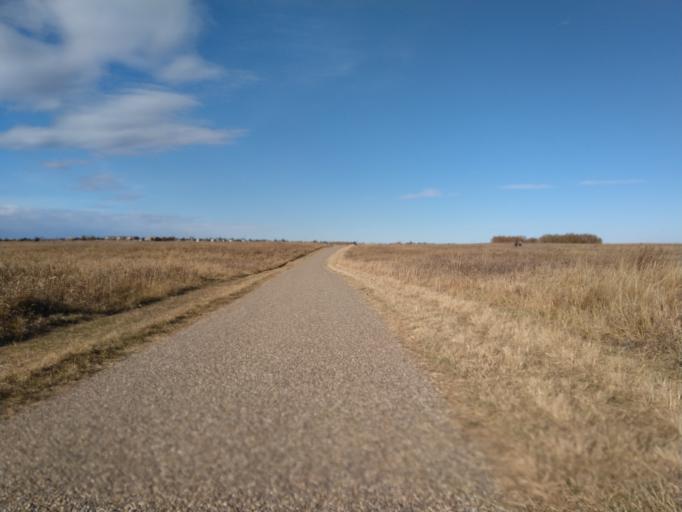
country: CA
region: Alberta
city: Calgary
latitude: 51.1174
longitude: -114.1264
